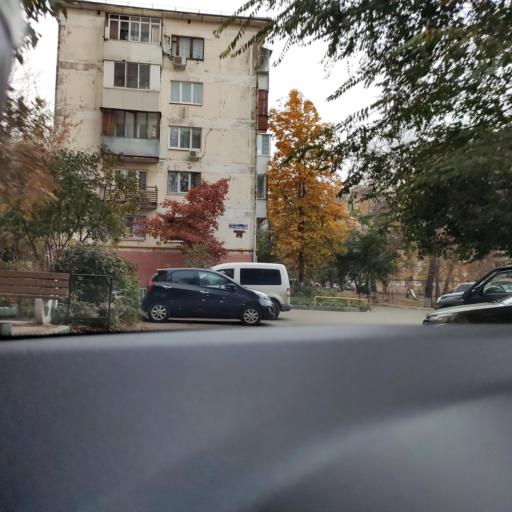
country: RU
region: Samara
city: Samara
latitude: 53.2452
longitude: 50.2429
